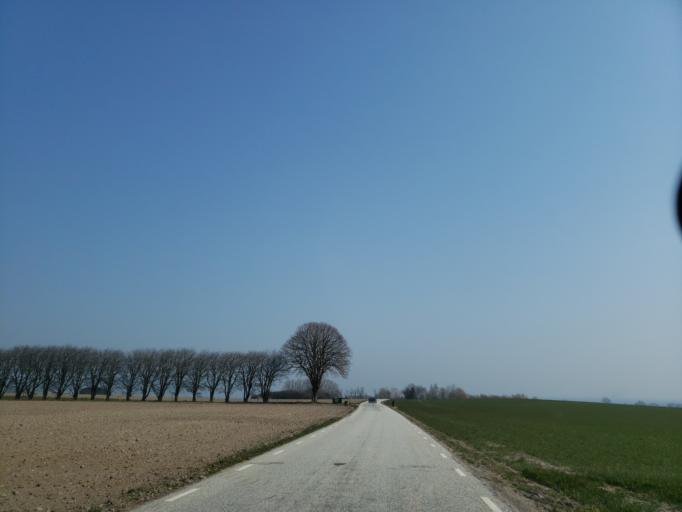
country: SE
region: Skane
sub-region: Simrishamns Kommun
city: Simrishamn
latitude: 55.5064
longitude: 14.3075
